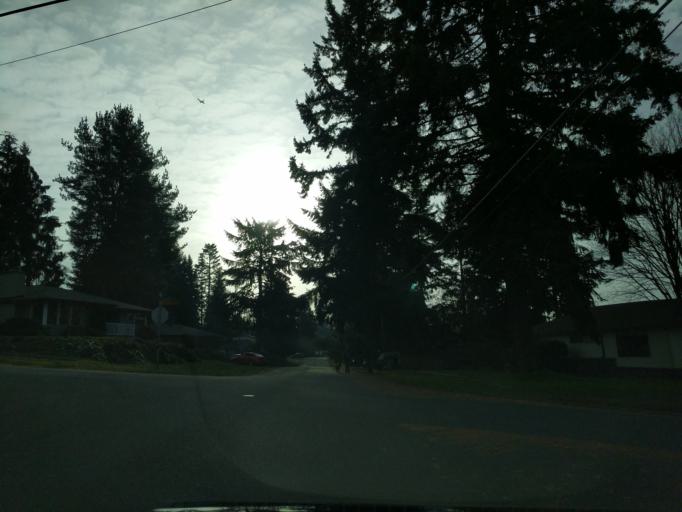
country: US
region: Washington
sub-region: King County
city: Shoreline
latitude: 47.7506
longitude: -122.3274
